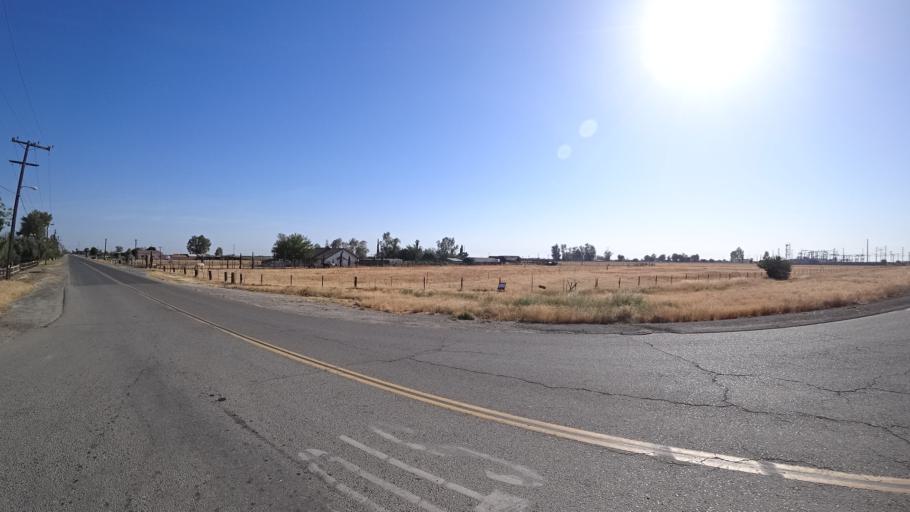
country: US
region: California
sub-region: Kings County
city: Corcoran
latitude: 36.1106
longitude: -119.5631
